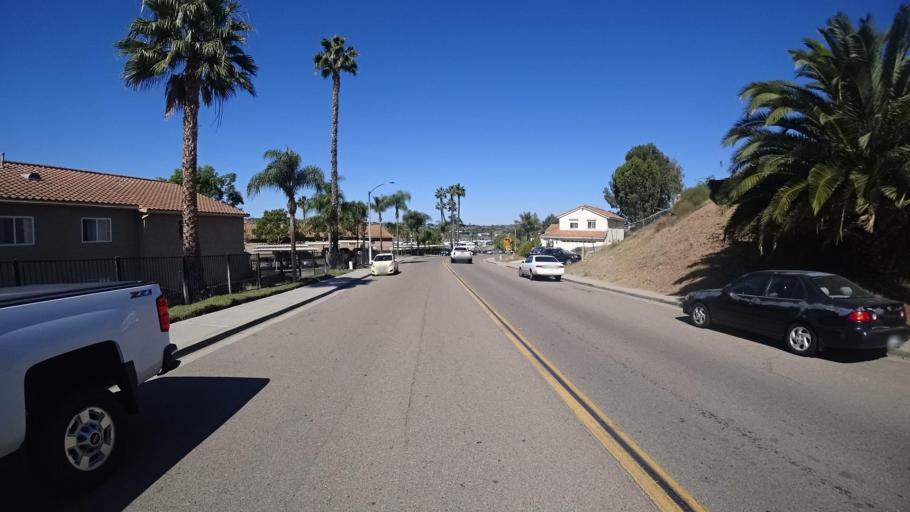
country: US
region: California
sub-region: San Diego County
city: La Presa
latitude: 32.6998
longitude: -117.0053
